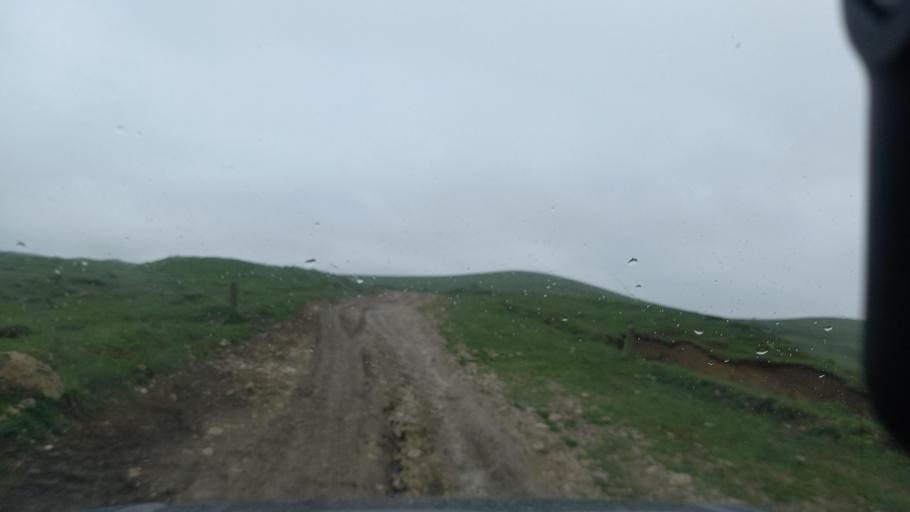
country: RU
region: Kabardino-Balkariya
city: Kamennomostskoye
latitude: 43.6937
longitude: 43.0055
